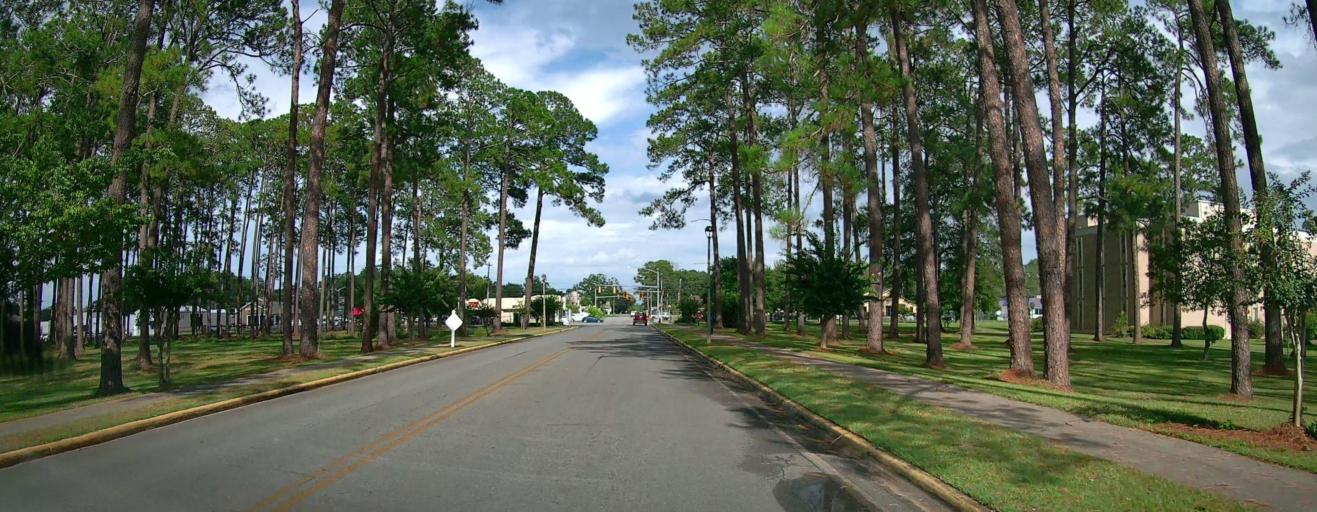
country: US
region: Georgia
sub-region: Coffee County
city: Douglas
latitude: 31.4971
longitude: -82.8524
